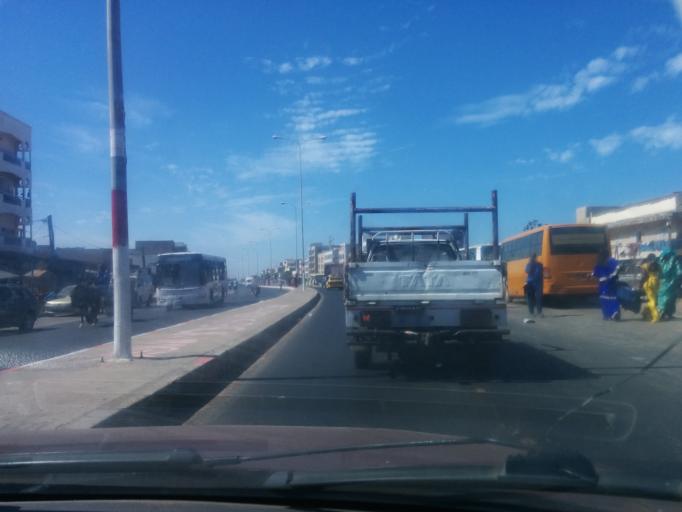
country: SN
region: Dakar
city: Pikine
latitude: 14.7767
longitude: -17.3947
